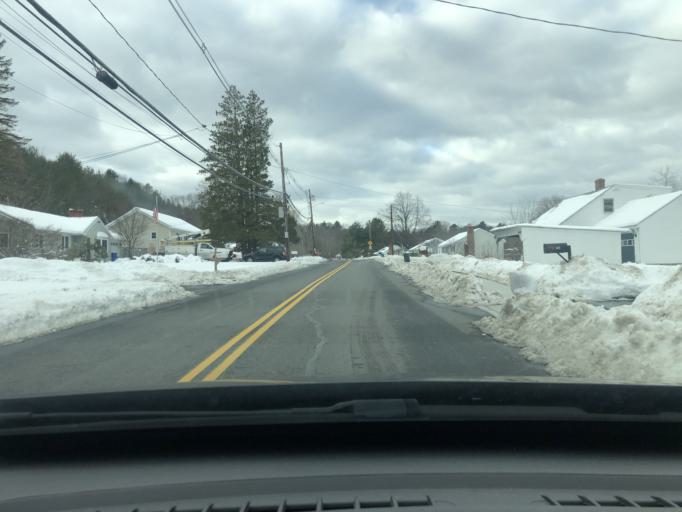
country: US
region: Massachusetts
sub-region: Middlesex County
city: Maynard
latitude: 42.4364
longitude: -71.4697
